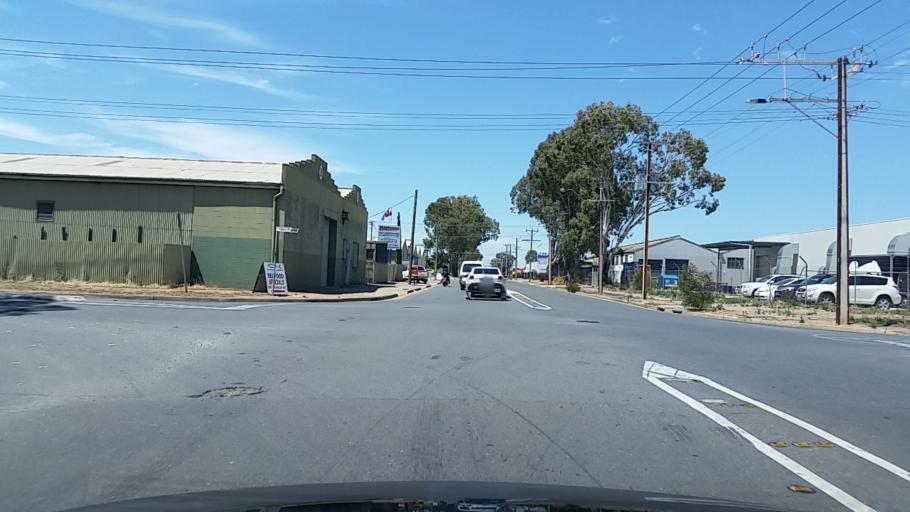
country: AU
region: South Australia
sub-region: Charles Sturt
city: Woodville North
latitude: -34.8458
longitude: 138.5464
